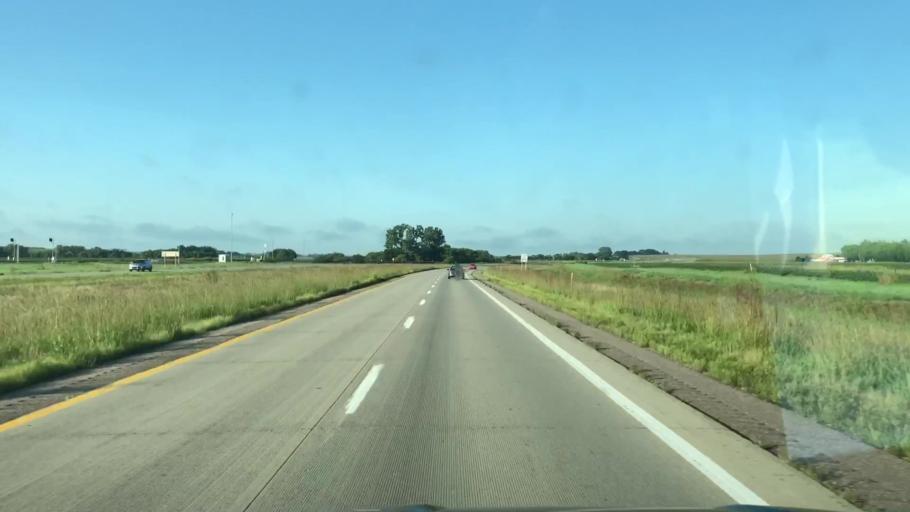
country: US
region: Iowa
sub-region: Sioux County
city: Alton
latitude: 42.9278
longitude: -96.0591
